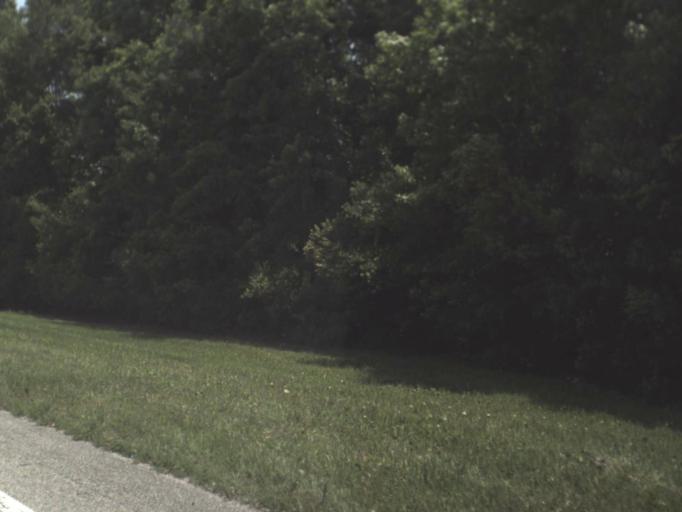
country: US
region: Florida
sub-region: Duval County
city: Baldwin
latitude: 30.1926
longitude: -82.0180
